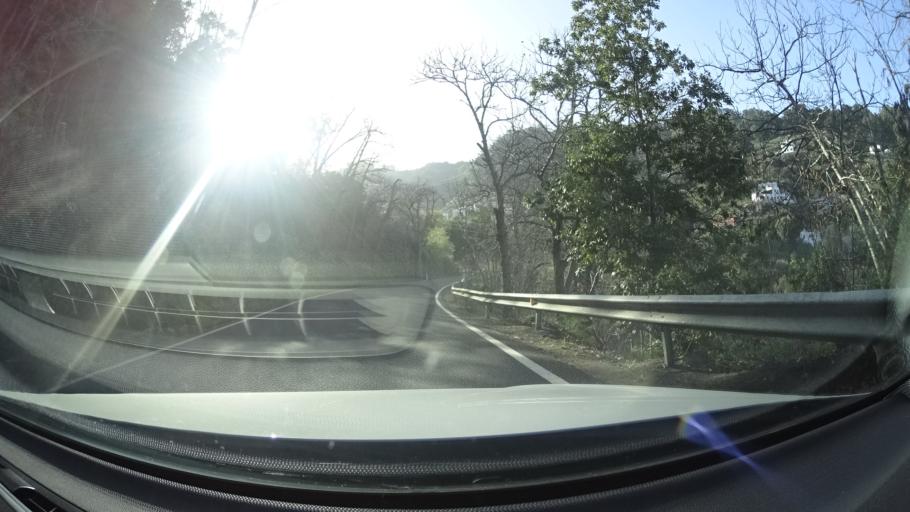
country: ES
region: Canary Islands
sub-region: Provincia de Las Palmas
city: Teror
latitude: 28.0574
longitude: -15.5570
